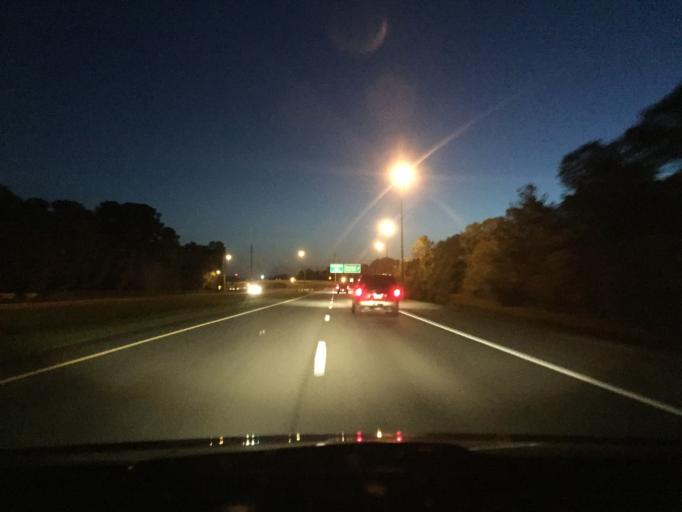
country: US
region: Georgia
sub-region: Chatham County
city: Isle of Hope
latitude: 31.9854
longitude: -81.0870
